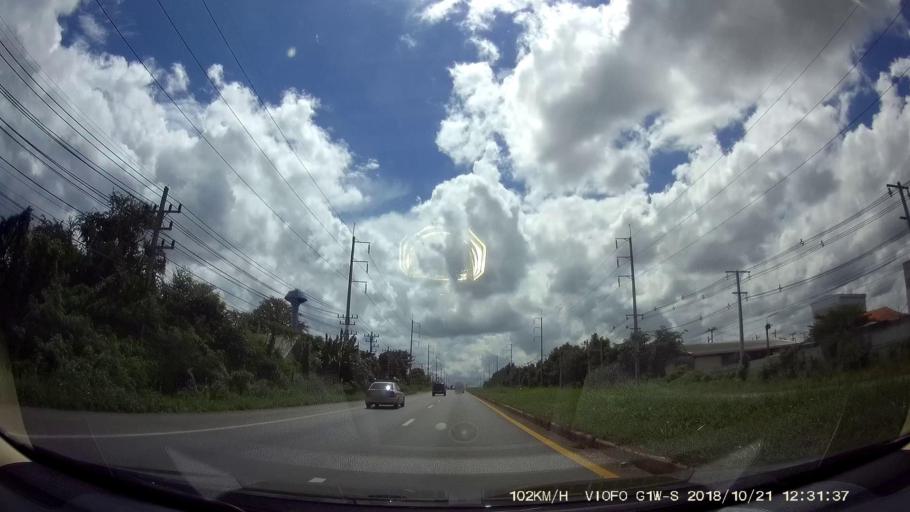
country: TH
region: Nakhon Ratchasima
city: Dan Khun Thot
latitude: 15.1539
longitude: 101.7341
